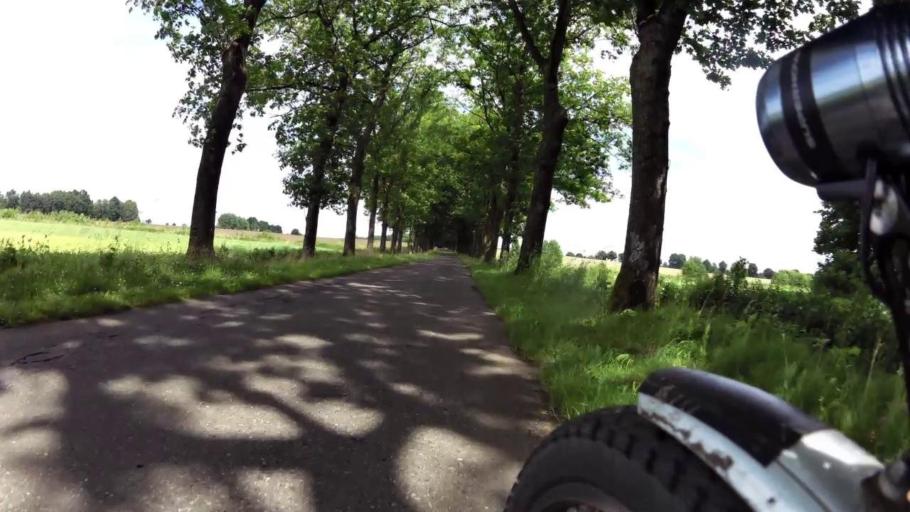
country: PL
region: West Pomeranian Voivodeship
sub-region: Powiat bialogardzki
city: Bialogard
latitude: 53.9440
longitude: 15.9869
